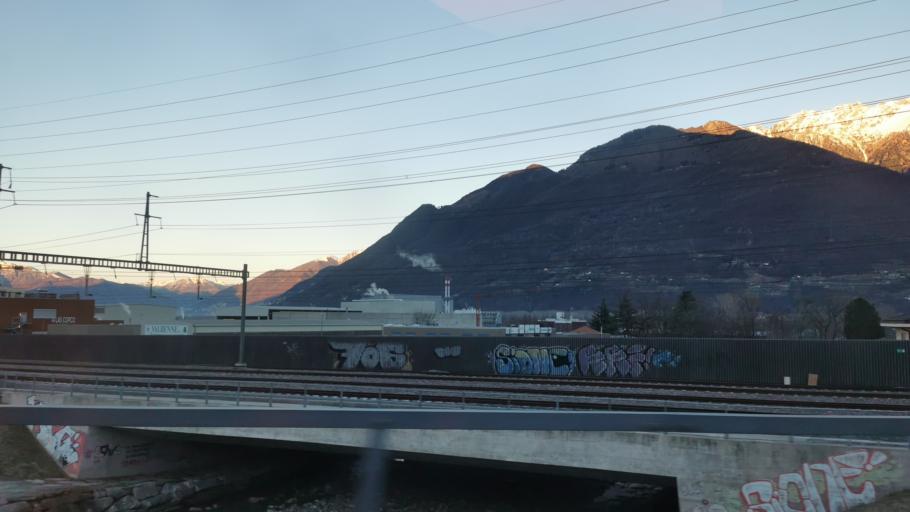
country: CH
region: Ticino
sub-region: Bellinzona District
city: Camorino
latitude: 46.1703
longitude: 8.9984
